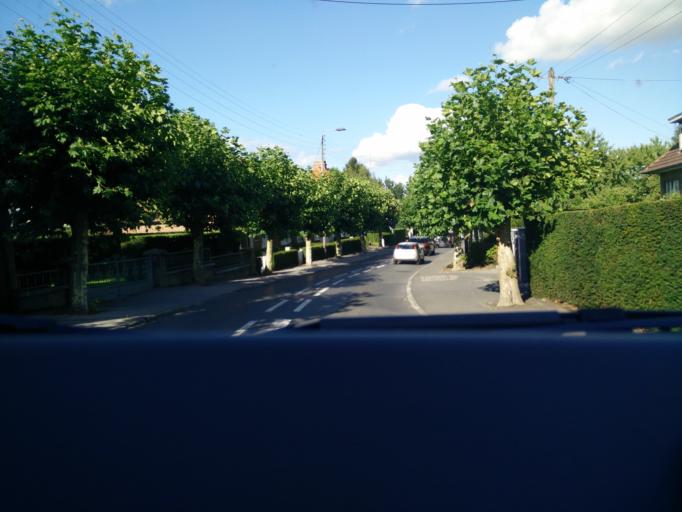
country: FR
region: Nord-Pas-de-Calais
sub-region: Departement du Nord
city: Maubeuge
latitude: 50.2838
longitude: 3.9771
